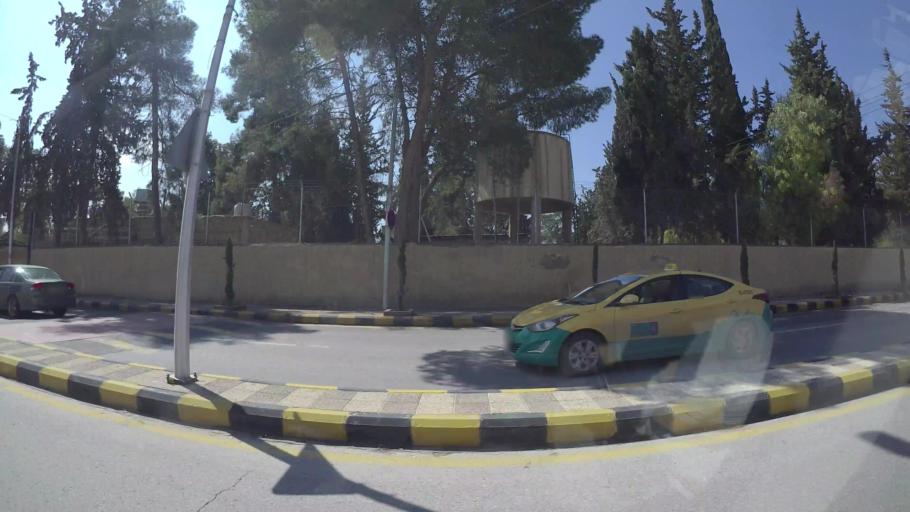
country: JO
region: Amman
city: Amman
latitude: 31.9770
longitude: 35.9819
